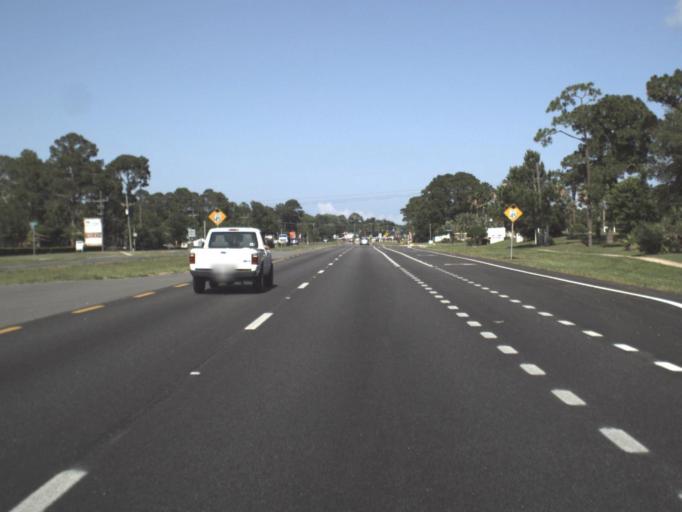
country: US
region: Florida
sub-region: Saint Johns County
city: Saint Augustine
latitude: 29.9163
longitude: -81.3533
